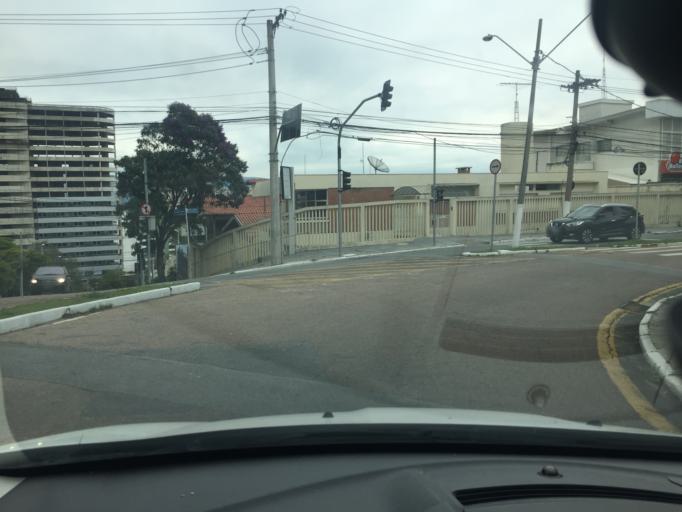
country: BR
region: Sao Paulo
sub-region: Jundiai
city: Jundiai
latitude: -23.1825
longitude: -46.8931
